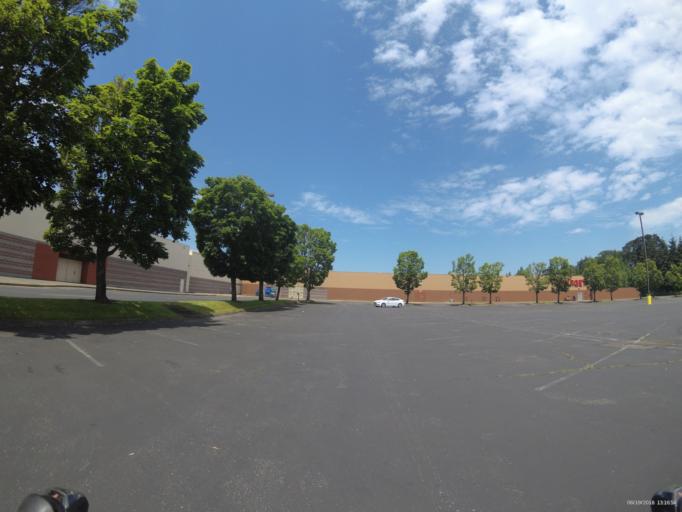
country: US
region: Washington
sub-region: Pierce County
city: Lakewood
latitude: 47.1621
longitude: -122.5118
